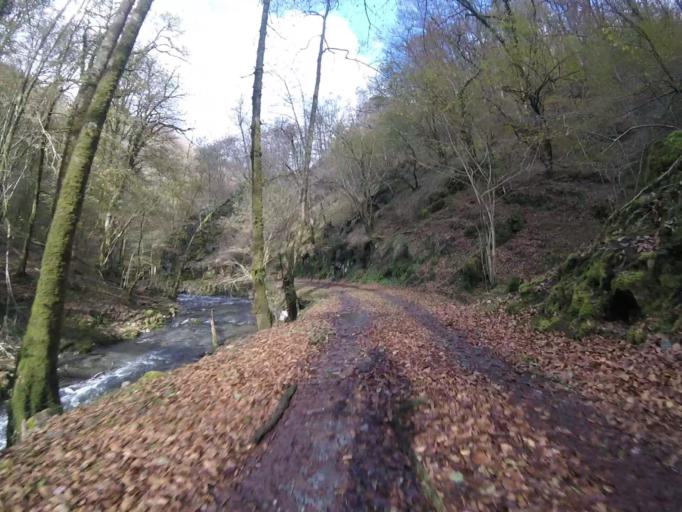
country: ES
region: Navarre
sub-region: Provincia de Navarra
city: Goizueta
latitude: 43.1870
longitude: -1.8013
